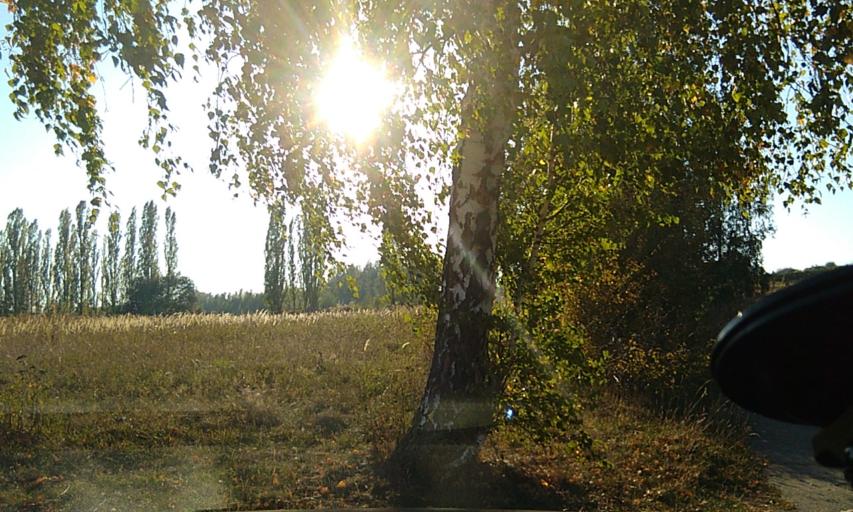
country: DE
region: Saxony
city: Wittgensdorf
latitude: 50.8484
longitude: 12.8736
